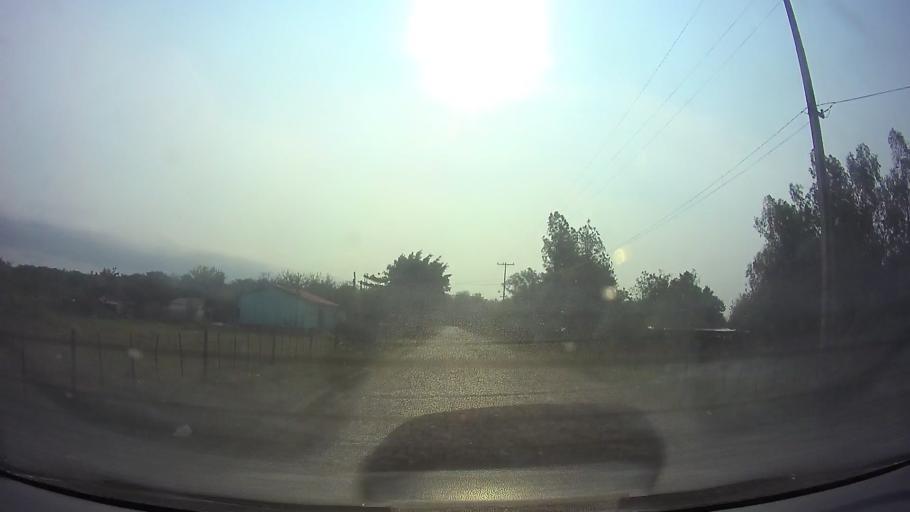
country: PY
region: Cordillera
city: Arroyos y Esteros
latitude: -25.0082
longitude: -57.1308
